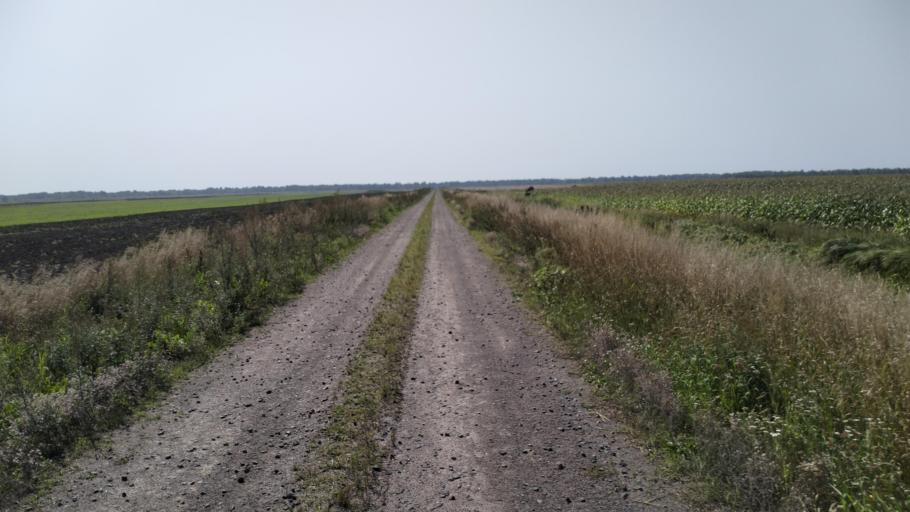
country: BY
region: Brest
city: Davyd-Haradok
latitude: 51.9855
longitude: 27.1638
